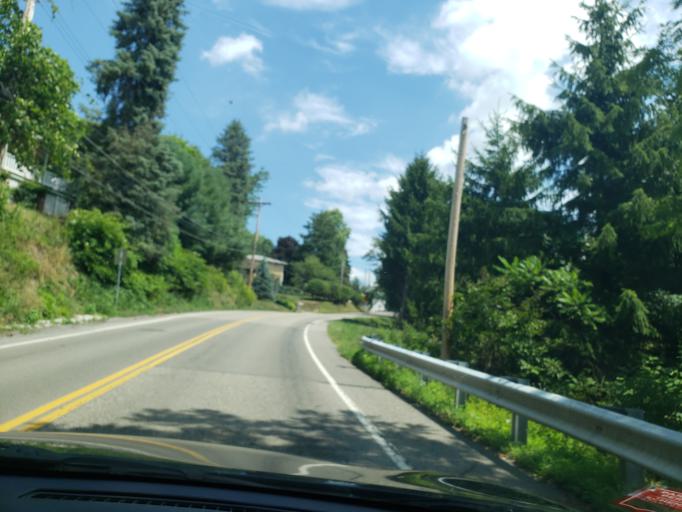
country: US
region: Pennsylvania
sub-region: Allegheny County
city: Coraopolis
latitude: 40.5393
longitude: -80.1560
